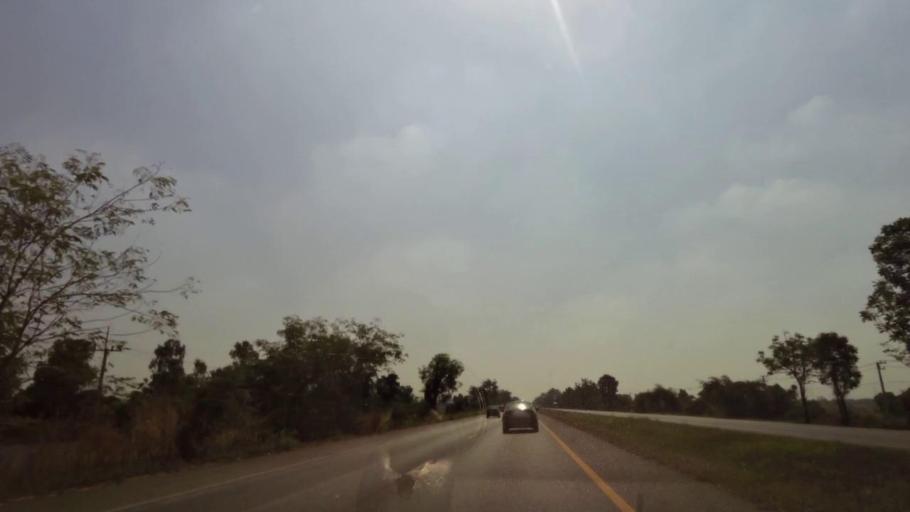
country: TH
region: Phichit
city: Wachira Barami
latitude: 16.4501
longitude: 100.1470
